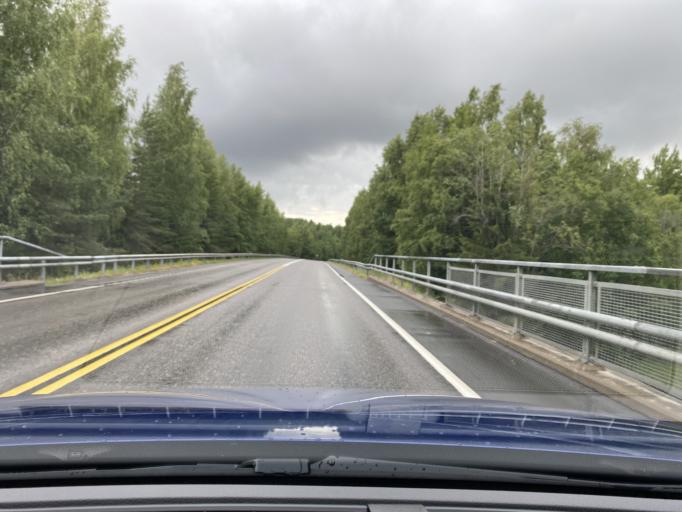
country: FI
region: Uusimaa
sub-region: Helsinki
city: Hyvinge
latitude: 60.5723
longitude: 24.8018
